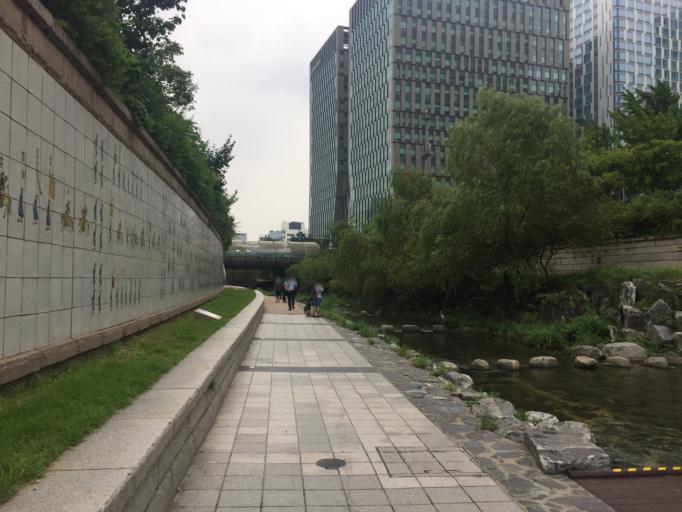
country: KR
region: Seoul
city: Seoul
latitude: 37.5682
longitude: 126.9863
